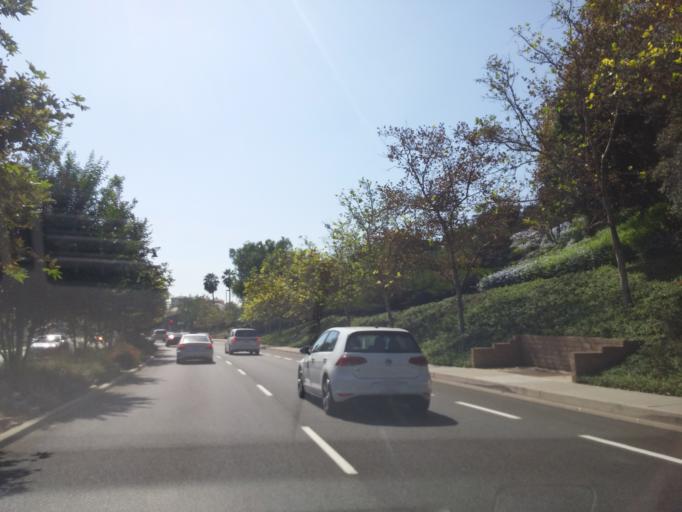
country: US
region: California
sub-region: Orange County
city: Mission Viejo
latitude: 33.5943
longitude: -117.6596
